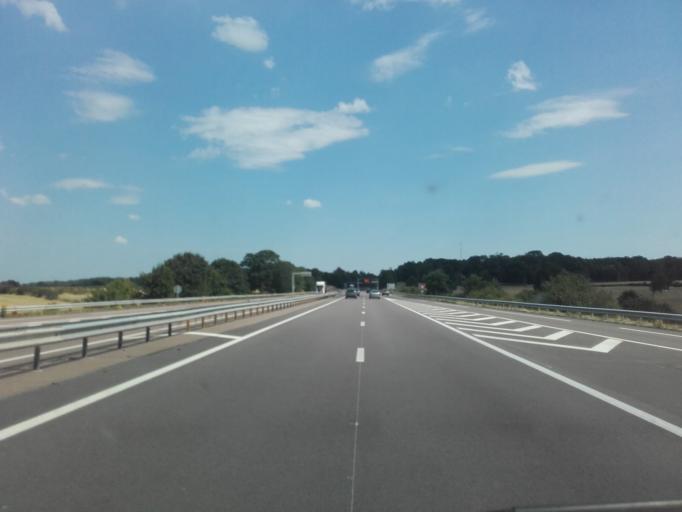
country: FR
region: Bourgogne
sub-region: Departement de la Cote-d'Or
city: Semur-en-Auxois
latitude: 47.4489
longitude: 4.2821
